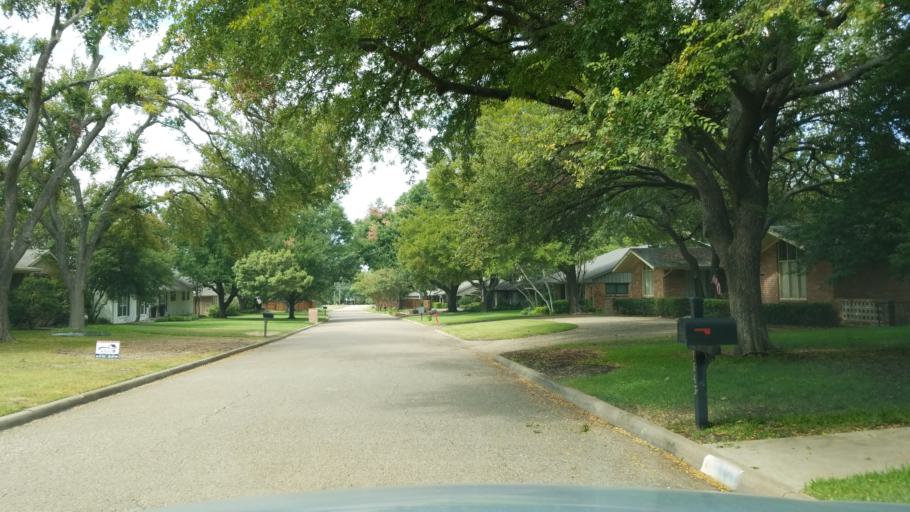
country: US
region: Texas
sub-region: Dallas County
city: Richardson
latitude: 32.9522
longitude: -96.7755
